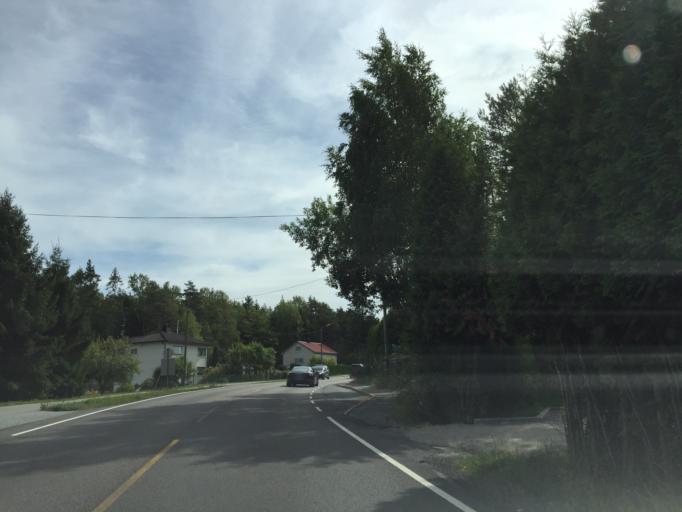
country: NO
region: Ostfold
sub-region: Fredrikstad
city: Fredrikstad
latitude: 59.1565
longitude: 10.9328
